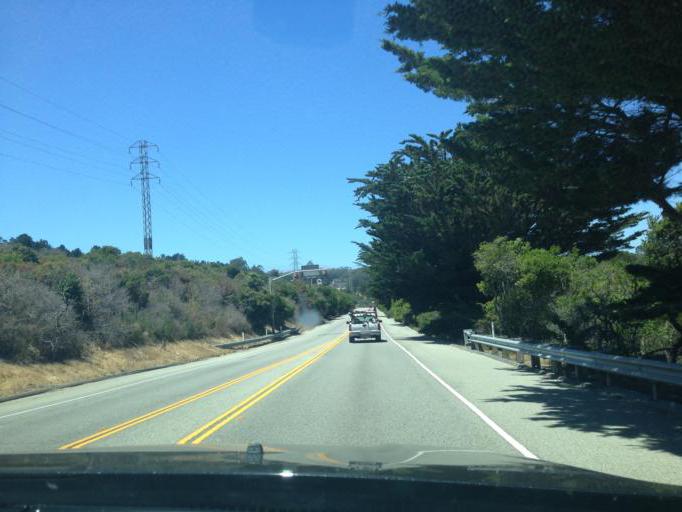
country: US
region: California
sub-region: San Mateo County
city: San Bruno
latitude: 37.6197
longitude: -122.4433
